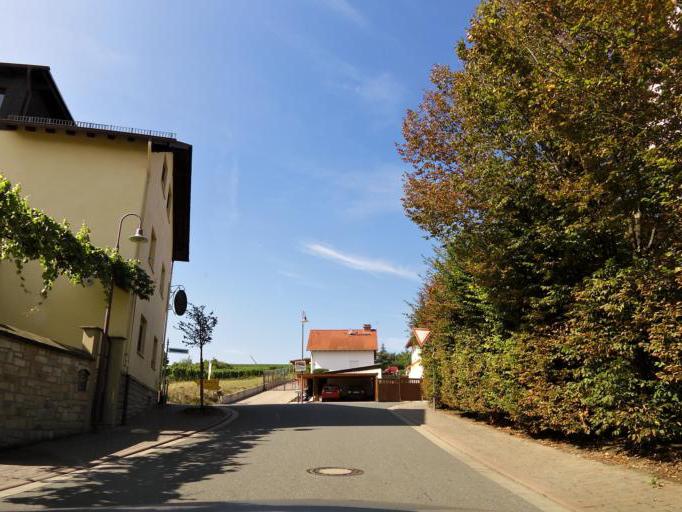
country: DE
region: Rheinland-Pfalz
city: Bechtolsheim
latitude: 49.8070
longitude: 8.1906
